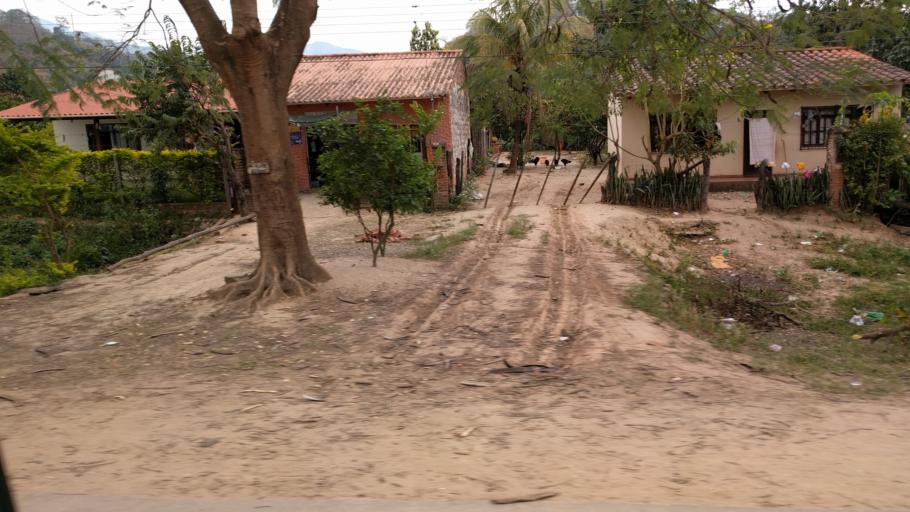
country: BO
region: Santa Cruz
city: Jorochito
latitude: -18.1574
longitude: -63.5006
